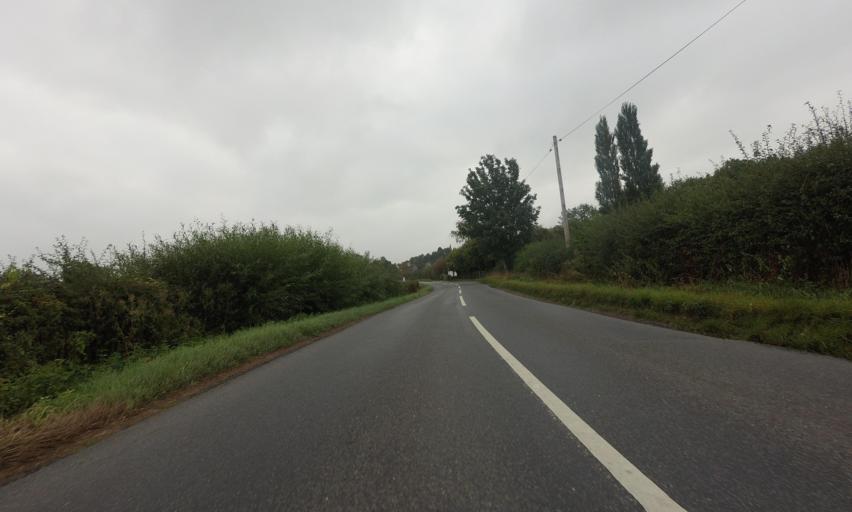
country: GB
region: England
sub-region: Gloucestershire
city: Winchcombe
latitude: 51.9731
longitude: -1.9979
